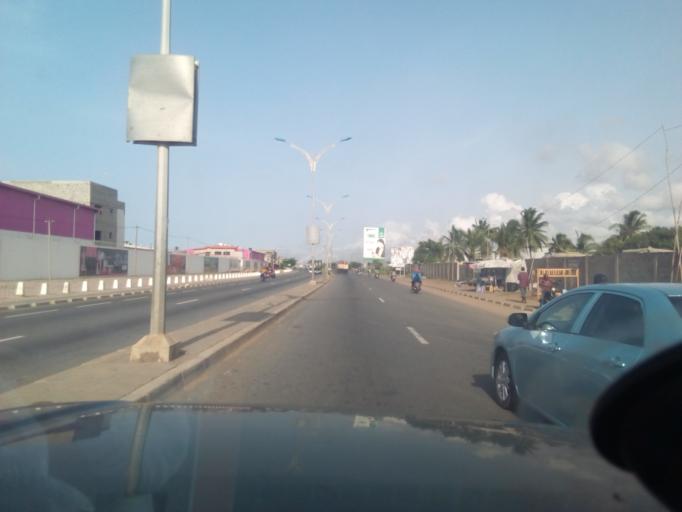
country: TG
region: Maritime
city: Lome
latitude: 6.1606
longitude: 1.3125
